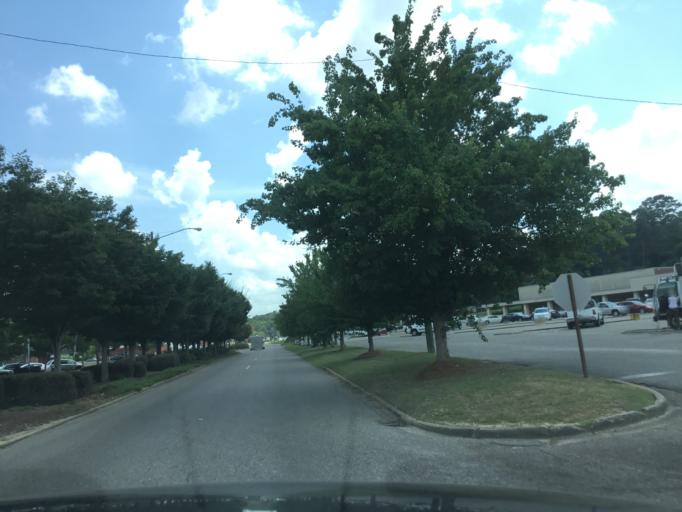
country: US
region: Alabama
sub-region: Montgomery County
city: Montgomery
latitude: 32.3912
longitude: -86.2575
